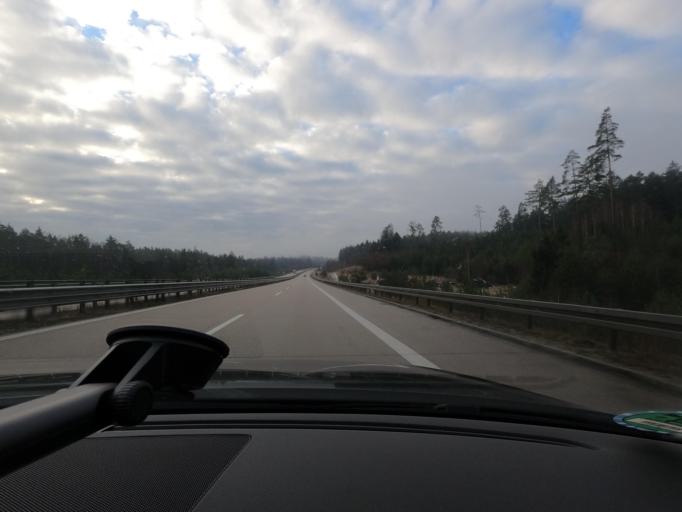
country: DE
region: Bavaria
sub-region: Upper Franconia
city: Niederfullbach
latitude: 50.2101
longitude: 11.0458
